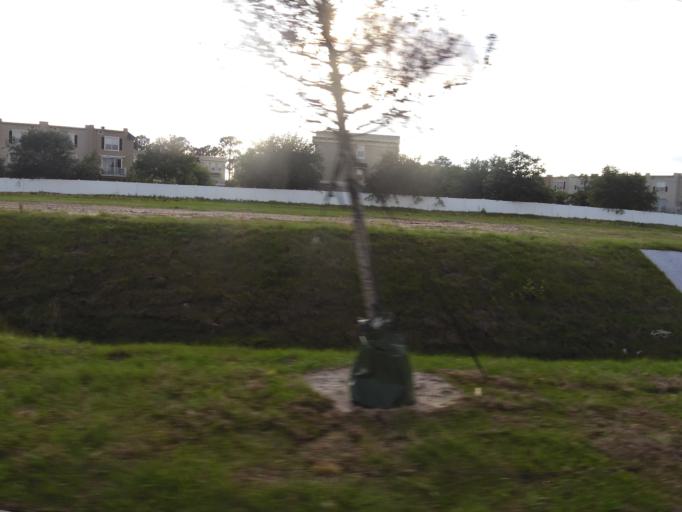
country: US
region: Florida
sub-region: Duval County
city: Jacksonville Beach
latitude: 30.2616
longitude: -81.5215
